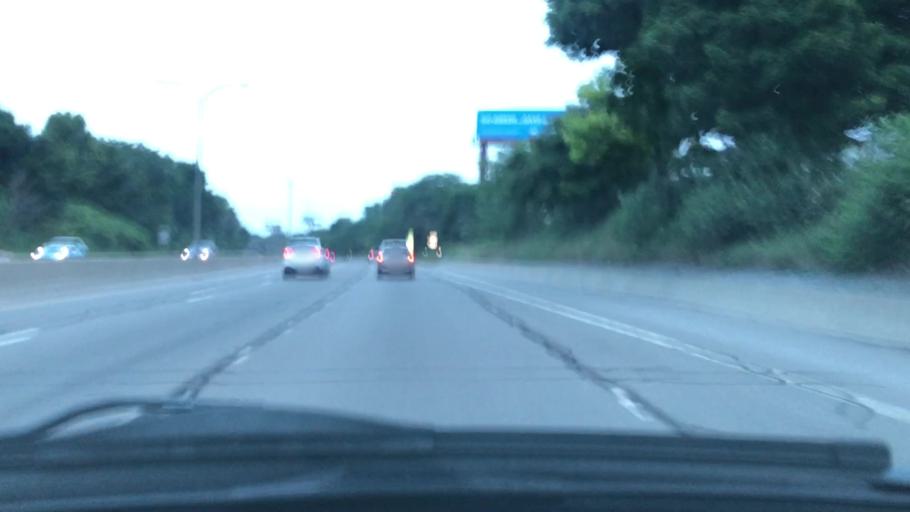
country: US
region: New York
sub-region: Erie County
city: Eggertsville
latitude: 42.9287
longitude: -78.8353
